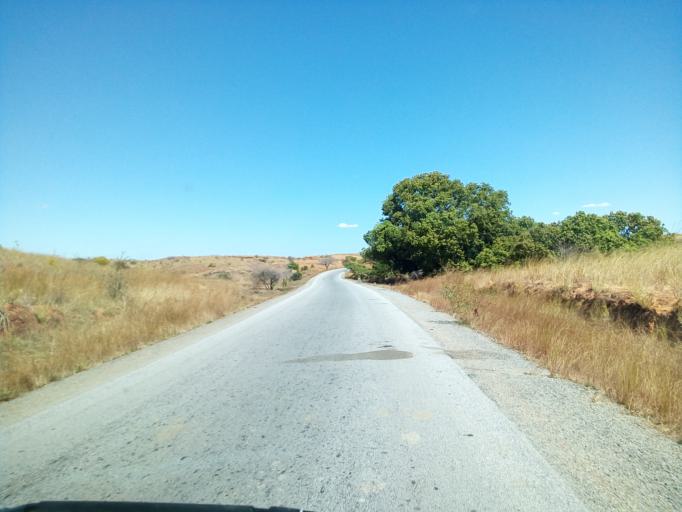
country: MG
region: Betsiboka
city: Maevatanana
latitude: -17.0954
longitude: 46.8132
